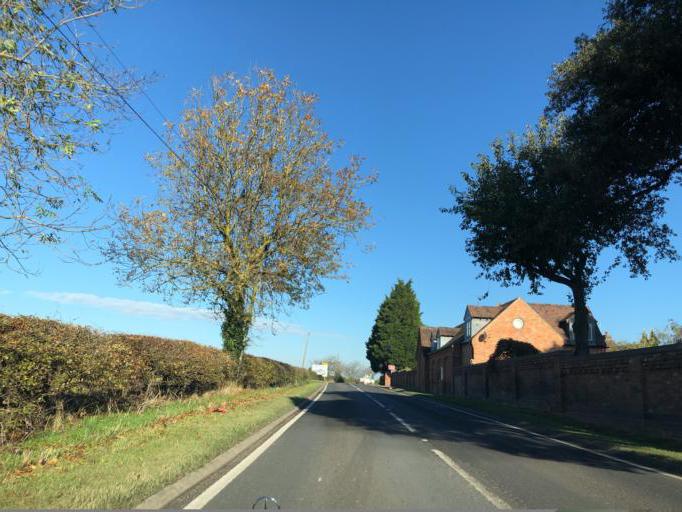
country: GB
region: England
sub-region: Warwickshire
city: Harbury
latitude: 52.2654
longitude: -1.4749
